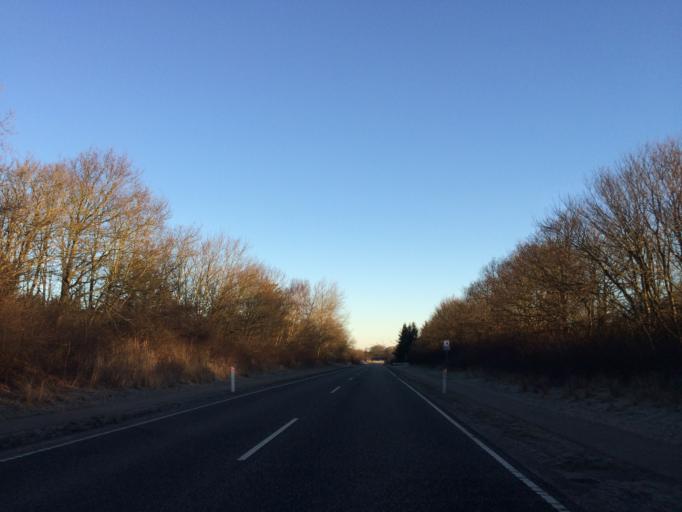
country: DK
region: Central Jutland
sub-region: Holstebro Kommune
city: Ulfborg
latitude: 56.3322
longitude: 8.3446
